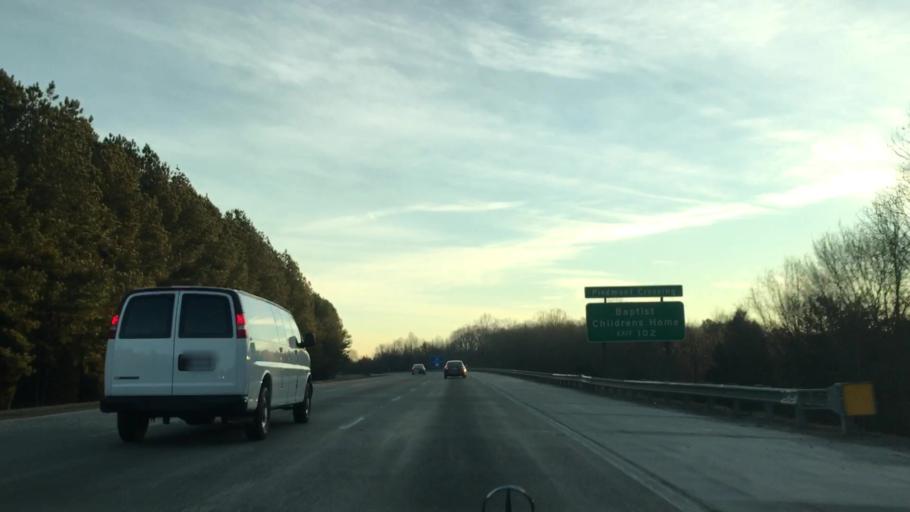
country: US
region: North Carolina
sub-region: Davidson County
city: Thomasville
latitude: 35.8497
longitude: -80.1174
